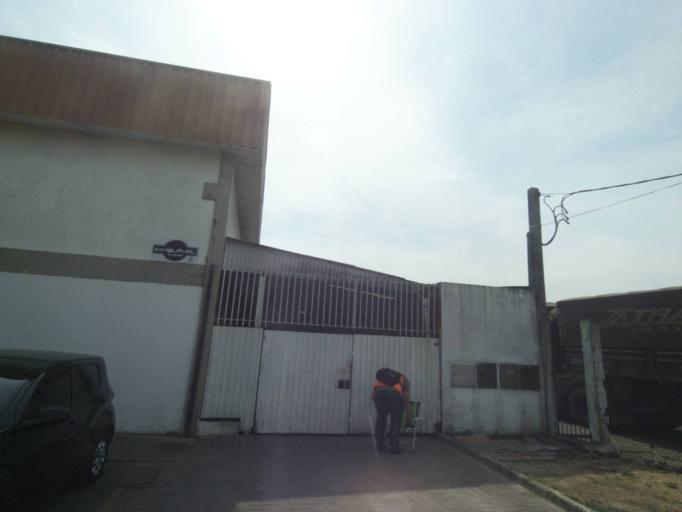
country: BR
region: Parana
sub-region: Paranagua
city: Paranagua
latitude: -25.5501
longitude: -48.5507
